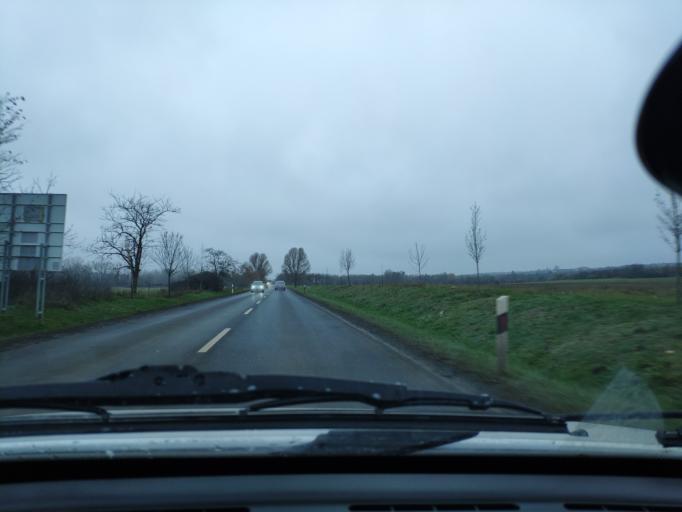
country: HU
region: Pest
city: Tarnok
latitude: 47.3947
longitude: 18.8457
